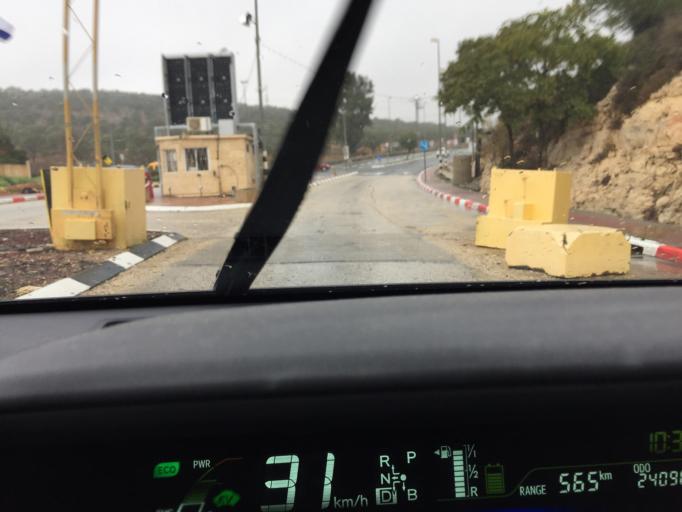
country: PS
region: West Bank
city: Kifil Haris
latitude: 32.1026
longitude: 35.1639
